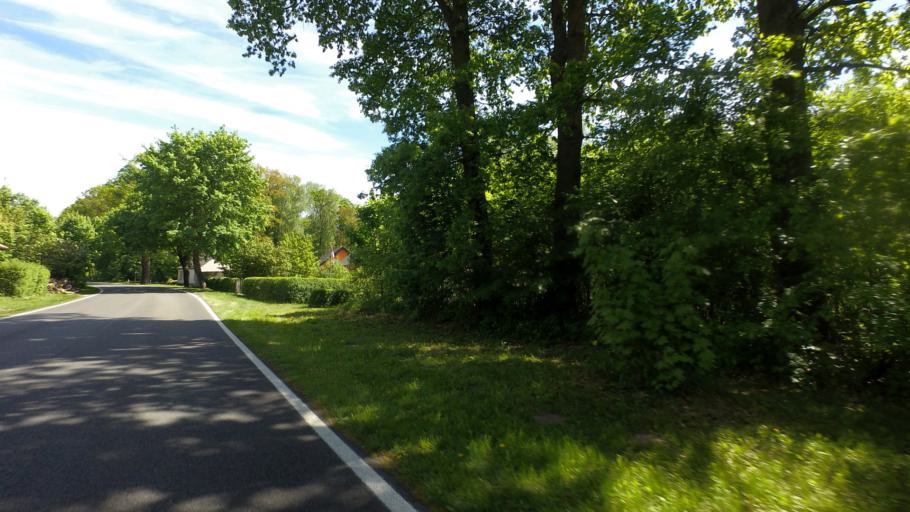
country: DE
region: Brandenburg
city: Sperenberg
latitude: 52.0462
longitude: 13.3862
